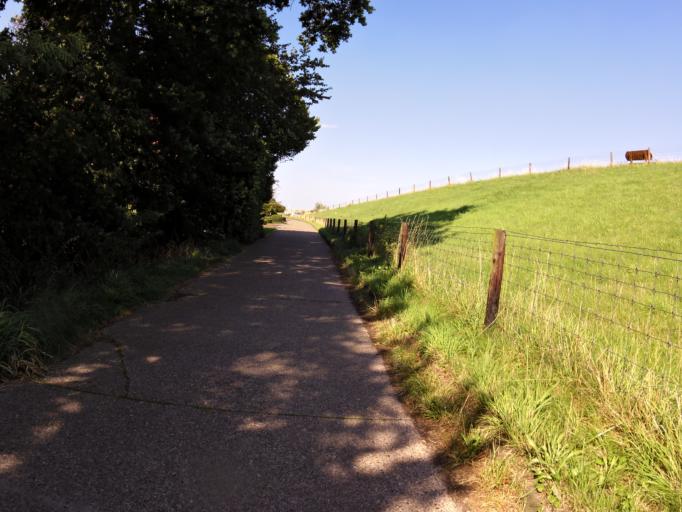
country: DE
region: Lower Saxony
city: Ovelgonne
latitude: 53.3834
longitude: 8.4587
